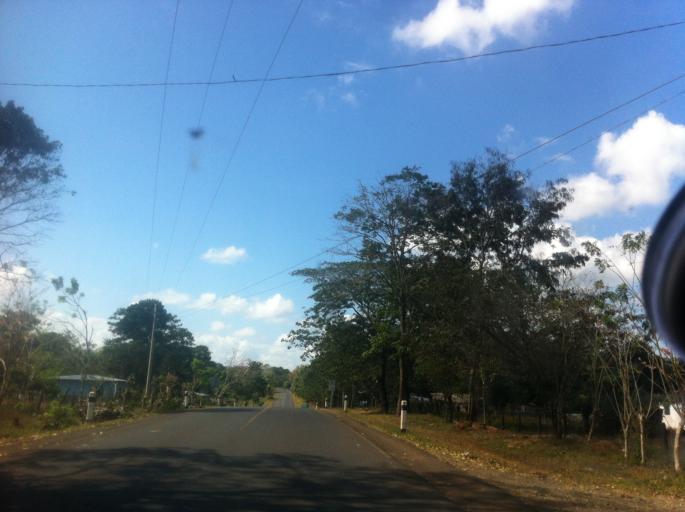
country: NI
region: Rio San Juan
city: San Carlos
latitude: 11.1917
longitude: -84.7432
